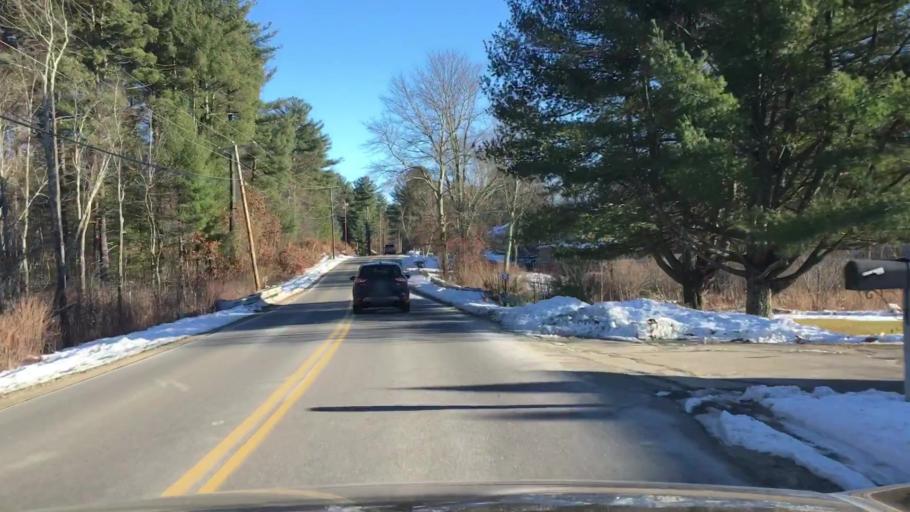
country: US
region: New Hampshire
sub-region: Hillsborough County
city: Hollis
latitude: 42.8129
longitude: -71.5661
